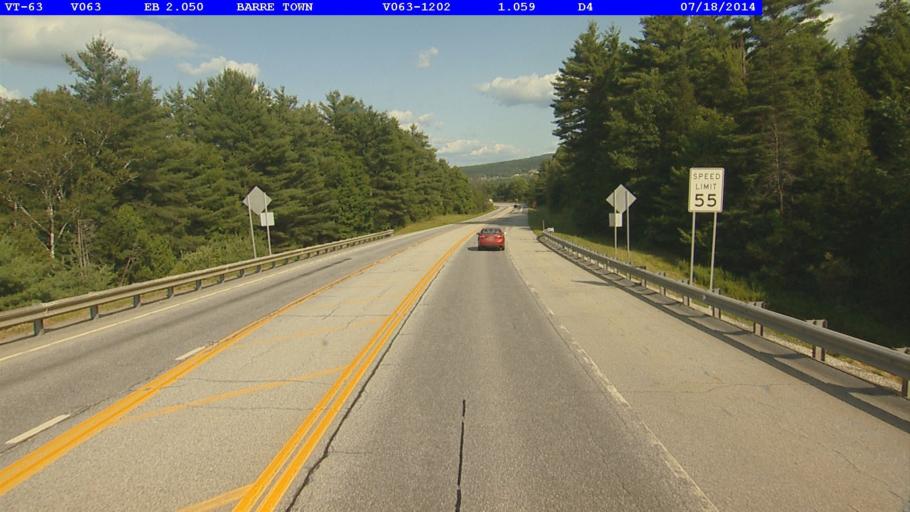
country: US
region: Vermont
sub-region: Washington County
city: South Barre
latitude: 44.1646
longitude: -72.5381
